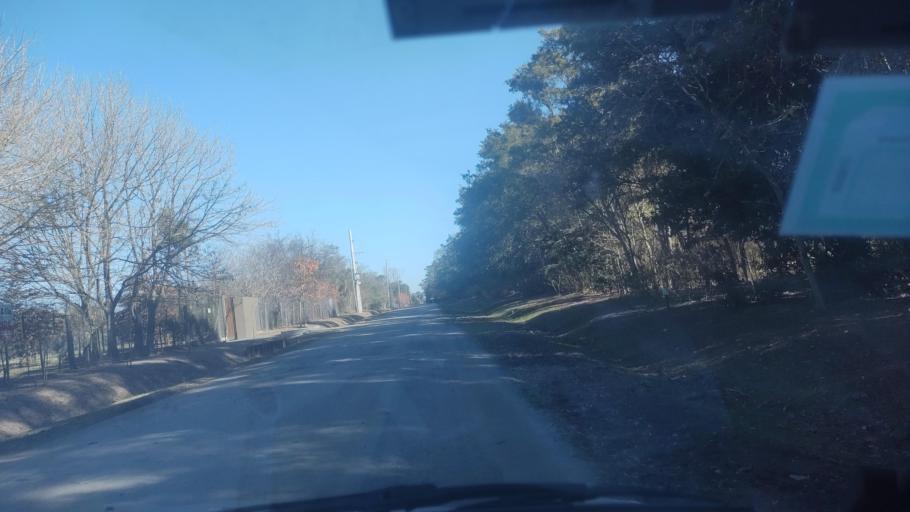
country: AR
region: Buenos Aires
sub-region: Partido de La Plata
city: La Plata
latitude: -34.8546
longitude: -58.1077
